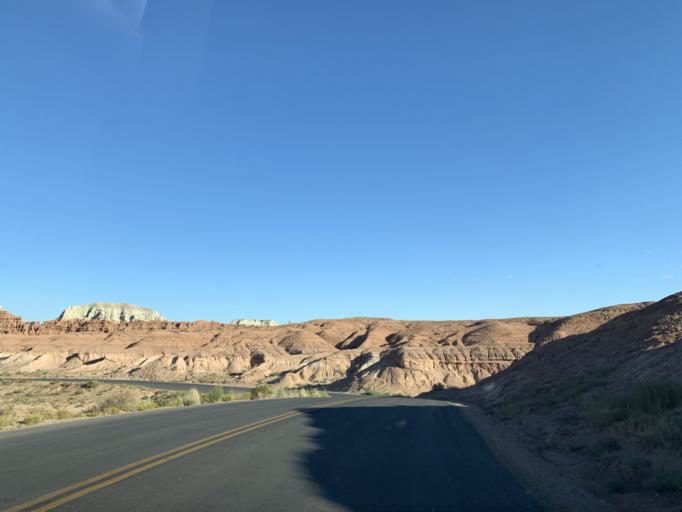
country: US
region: Utah
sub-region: Emery County
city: Ferron
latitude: 38.5674
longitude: -110.7048
